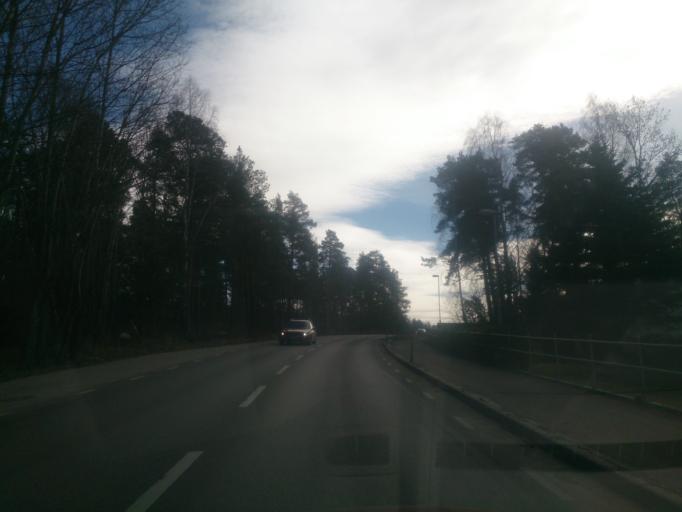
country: SE
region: OEstergoetland
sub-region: Norrkopings Kommun
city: Kimstad
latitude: 58.5572
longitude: 15.9520
